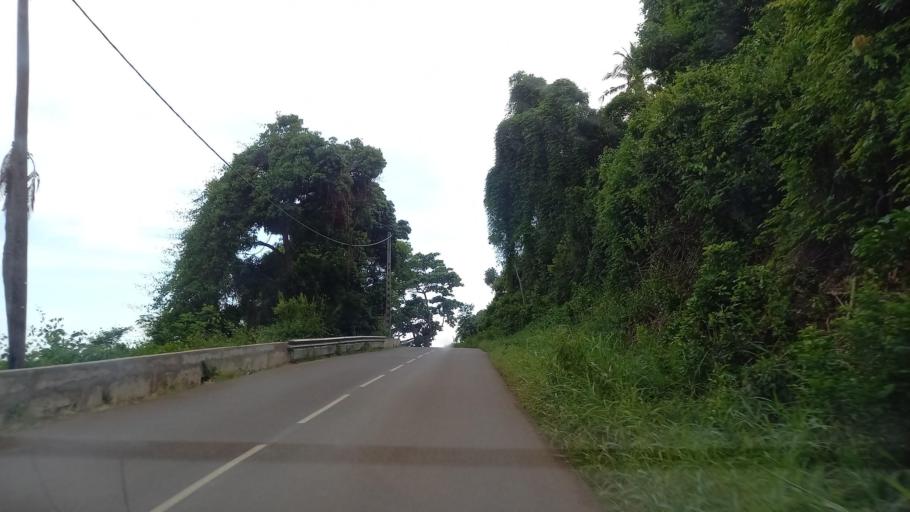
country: YT
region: M'Tsangamouji
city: M'Tsangamouji
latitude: -12.7641
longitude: 45.0805
